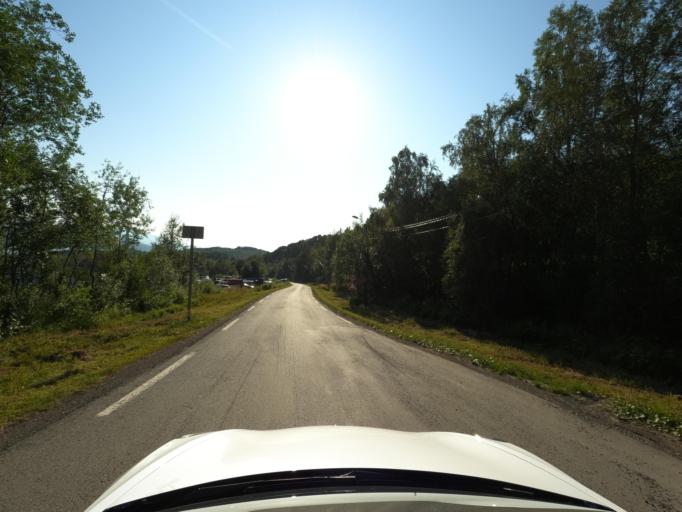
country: NO
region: Nordland
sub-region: Narvik
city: Bjerkvik
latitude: 68.4760
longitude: 17.5169
